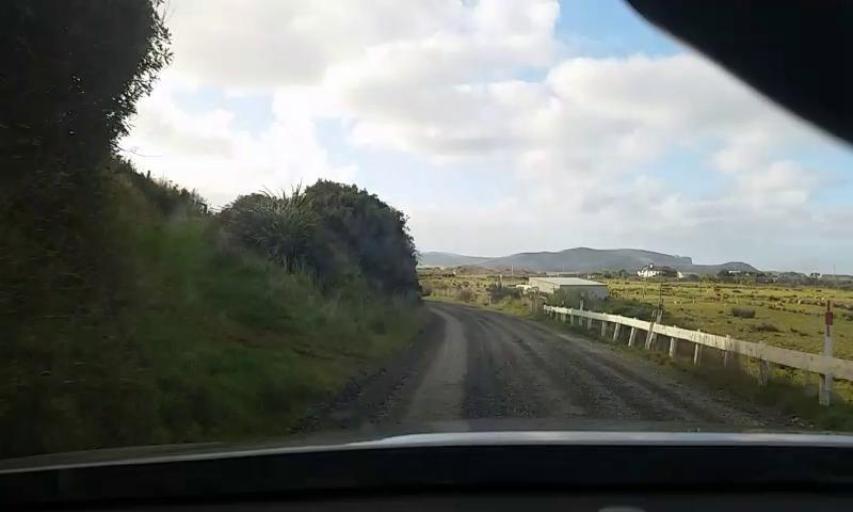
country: NZ
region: Otago
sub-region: Clutha District
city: Papatowai
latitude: -46.6518
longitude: 169.0966
